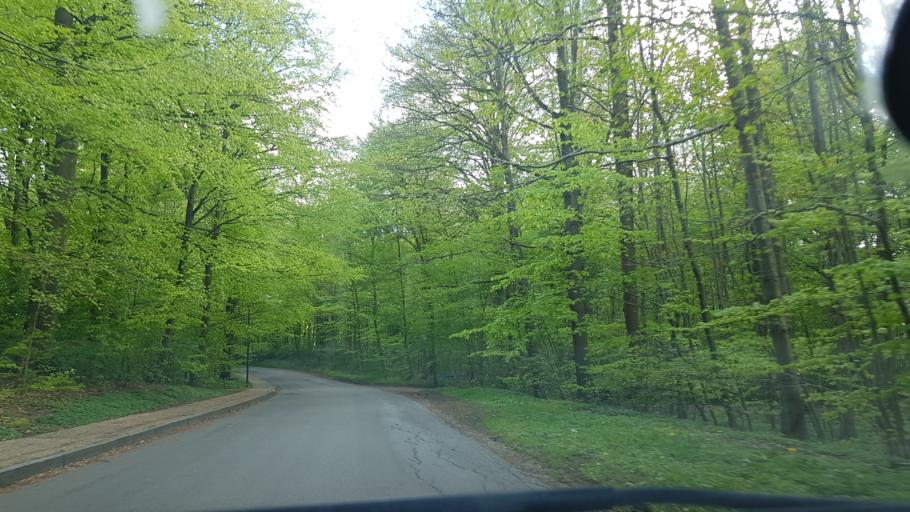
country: DK
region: Capital Region
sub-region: Rudersdal Kommune
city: Holte
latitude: 55.8229
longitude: 12.4578
